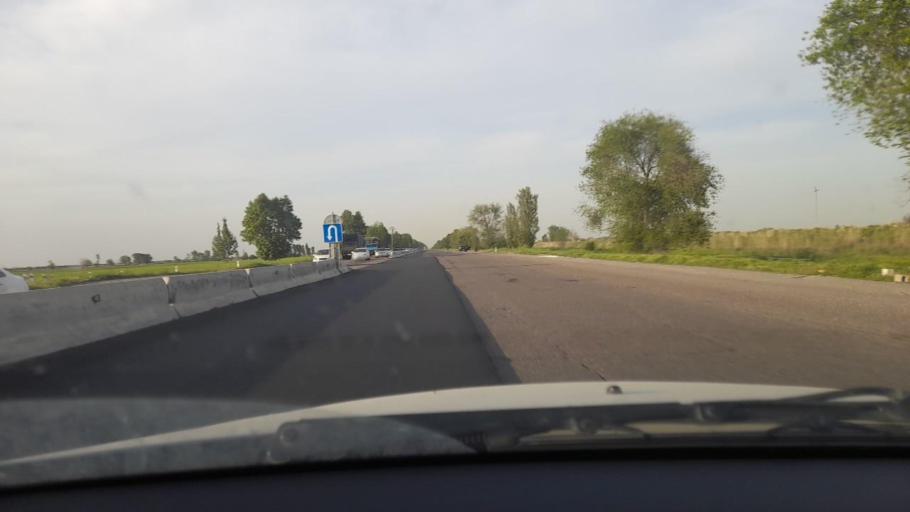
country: UZ
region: Jizzax
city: Gagarin
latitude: 40.5226
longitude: 68.3340
